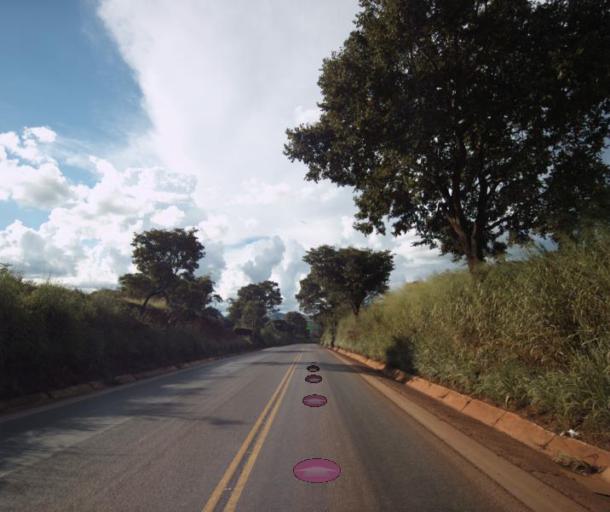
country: BR
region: Goias
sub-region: Rialma
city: Rialma
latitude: -15.3169
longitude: -49.5724
